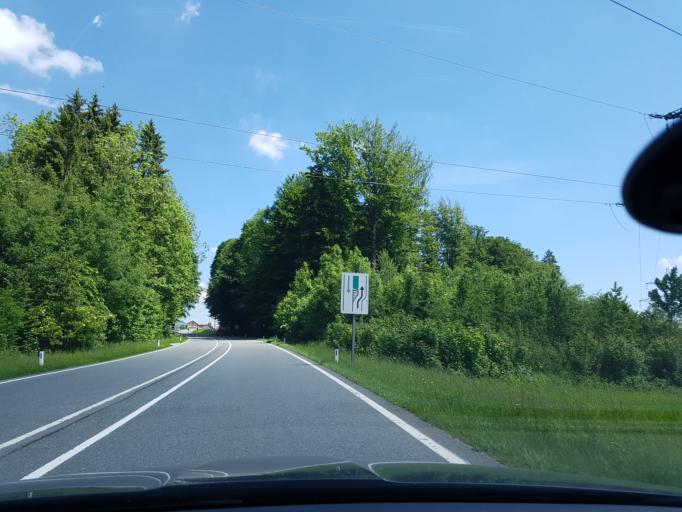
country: AT
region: Salzburg
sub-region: Politischer Bezirk Salzburg-Umgebung
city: Elixhausen
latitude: 47.8872
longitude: 13.0695
